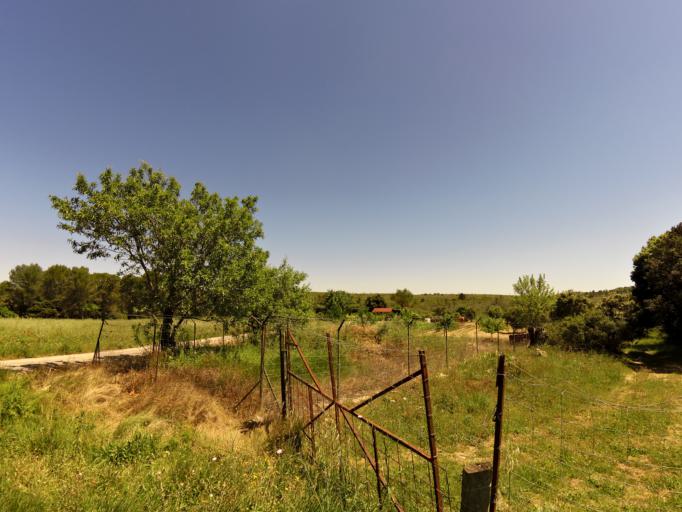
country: FR
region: Languedoc-Roussillon
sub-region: Departement de l'Herault
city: Assas
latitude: 43.7112
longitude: 3.9060
